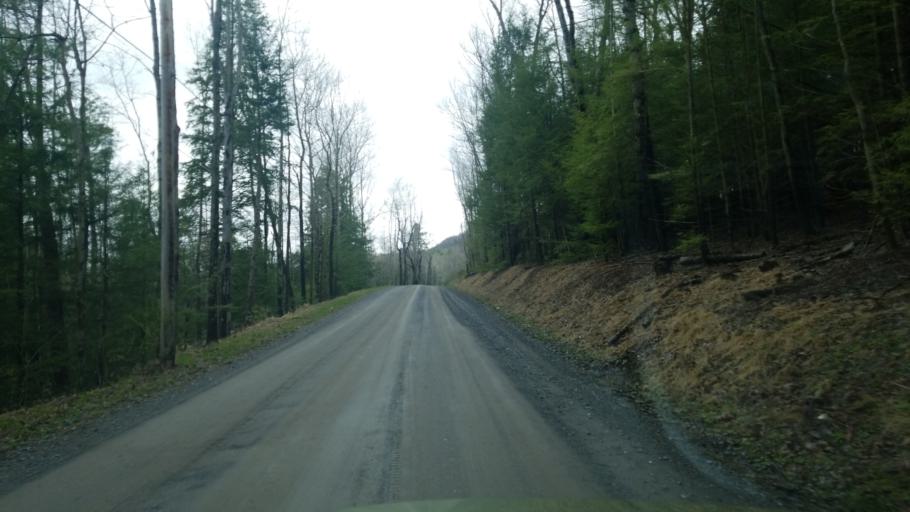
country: US
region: Pennsylvania
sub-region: Clearfield County
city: Shiloh
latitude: 41.1195
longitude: -78.3410
